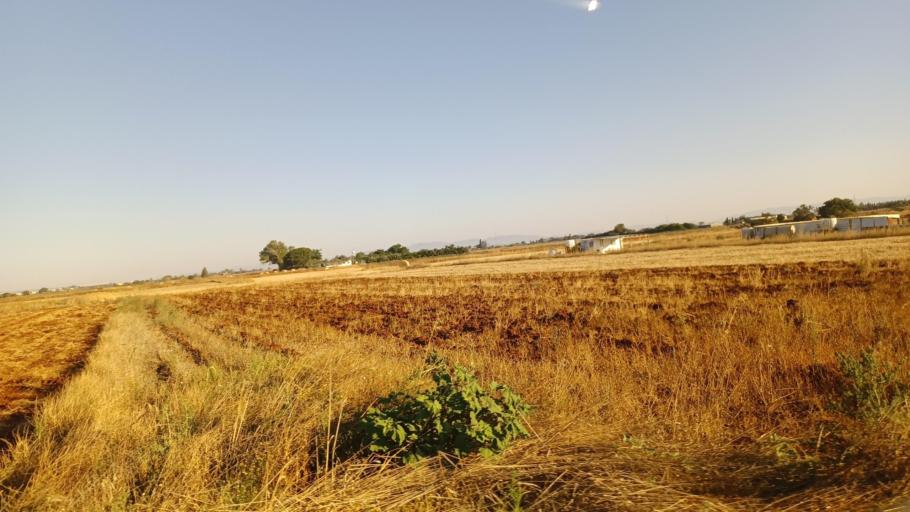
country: CY
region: Ammochostos
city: Avgorou
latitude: 35.0066
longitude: 33.8302
